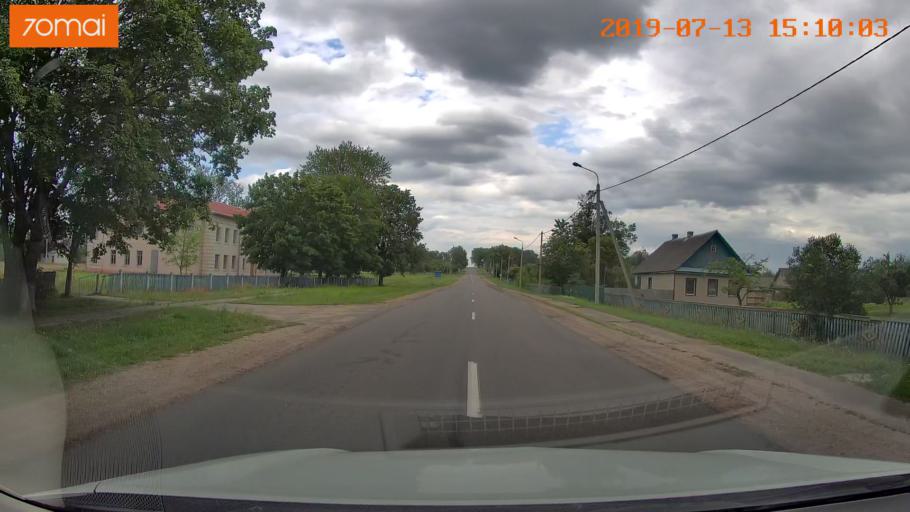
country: BY
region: Mogilev
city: Hlusha
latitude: 53.1711
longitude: 28.7706
